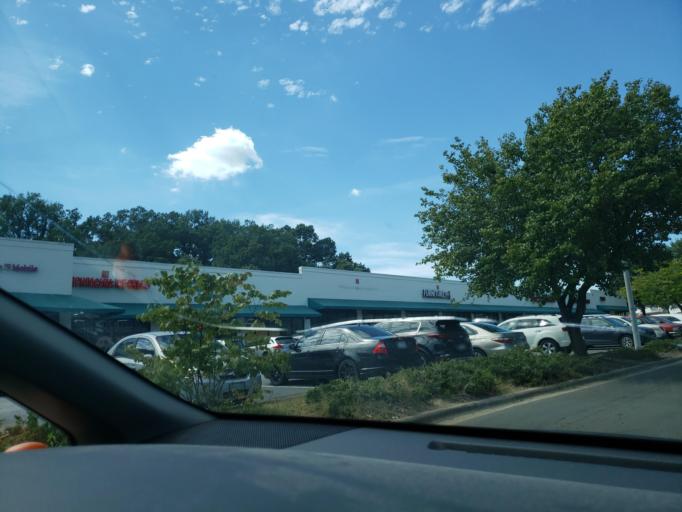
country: US
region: North Carolina
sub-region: Durham County
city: Durham
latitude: 36.0176
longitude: -78.8873
